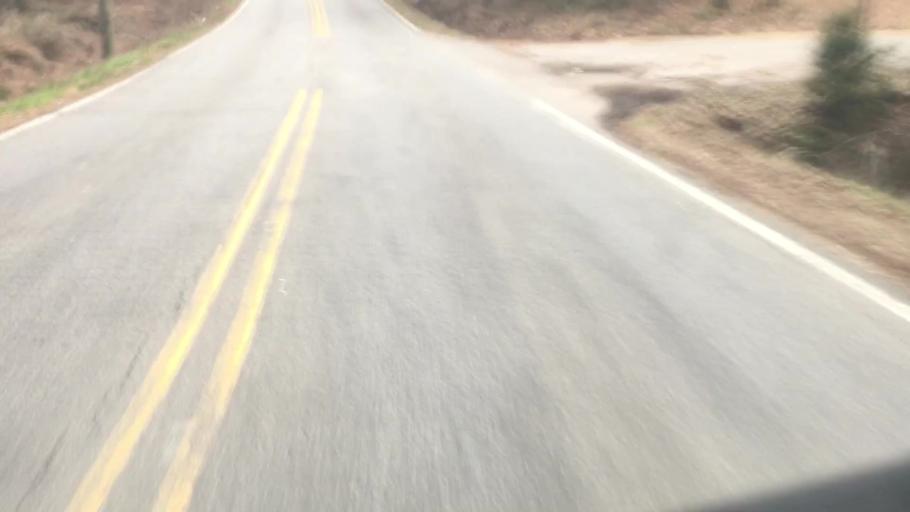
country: US
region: Alabama
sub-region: Jefferson County
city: Cahaba Heights
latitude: 33.4208
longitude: -86.7473
